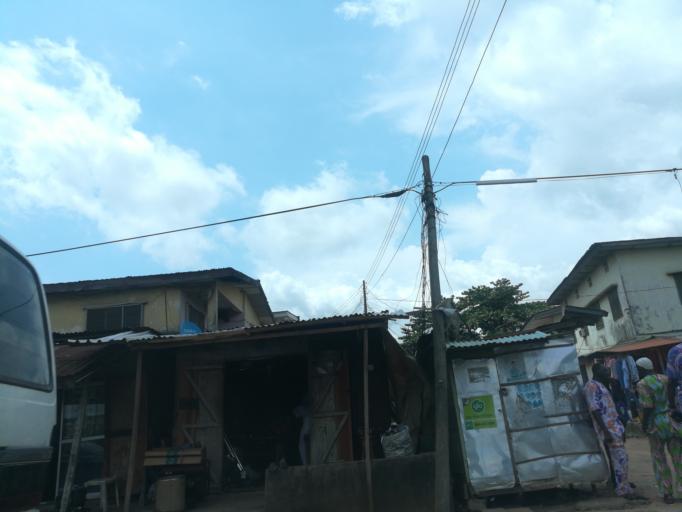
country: NG
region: Lagos
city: Somolu
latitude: 6.5395
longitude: 3.3646
